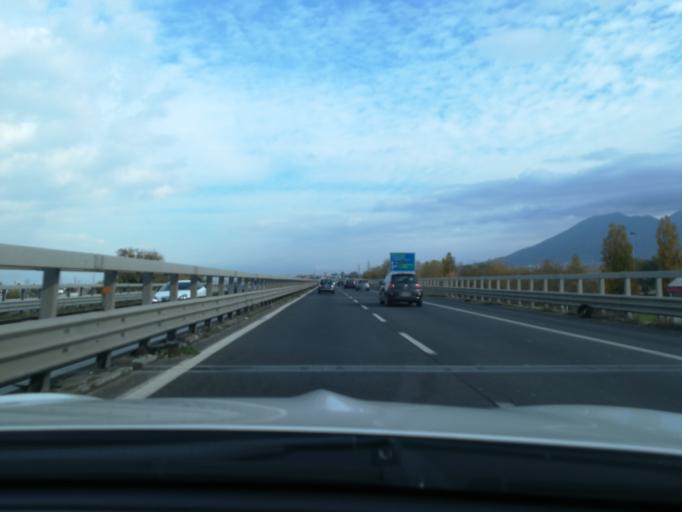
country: IT
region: Campania
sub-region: Provincia di Napoli
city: Arpino
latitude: 40.8657
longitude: 14.3089
